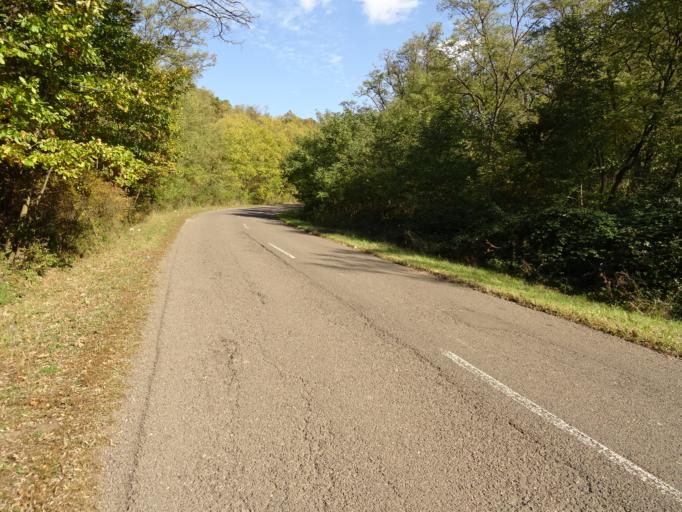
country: HU
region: Nograd
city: Salgotarjan
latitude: 48.0502
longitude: 19.7537
